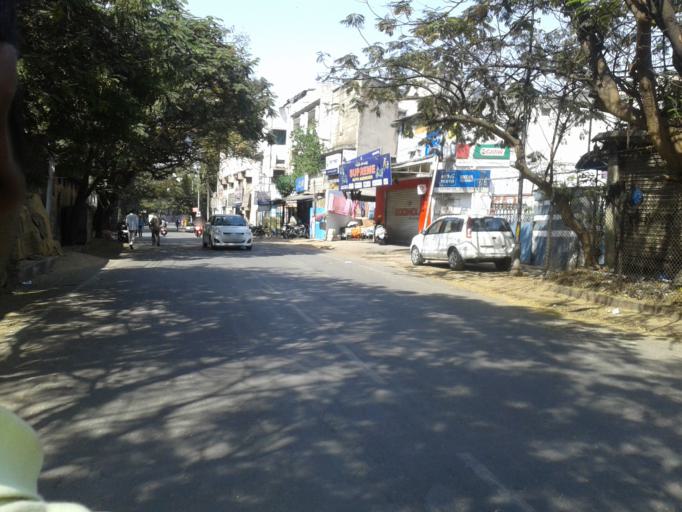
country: IN
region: Telangana
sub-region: Hyderabad
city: Hyderabad
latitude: 17.3905
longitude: 78.4853
